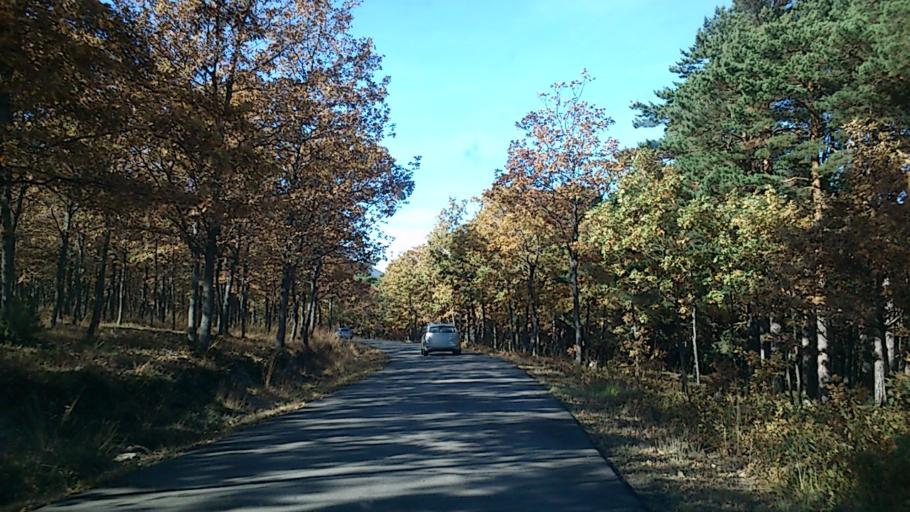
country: ES
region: Aragon
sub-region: Provincia de Zaragoza
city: Lituenigo
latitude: 41.8102
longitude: -1.8059
